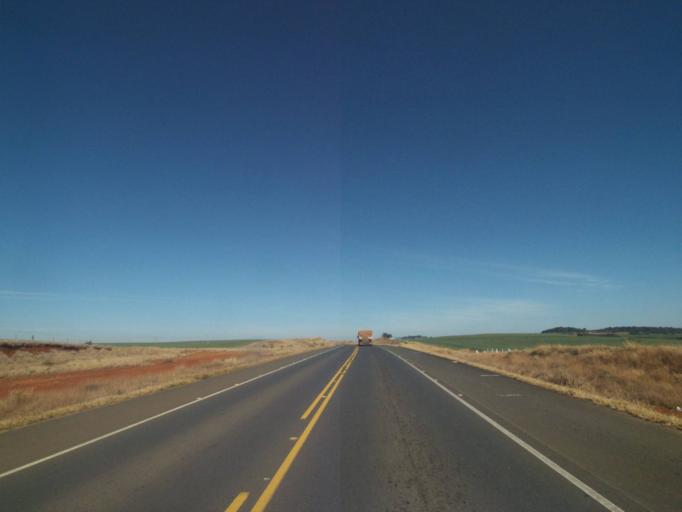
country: BR
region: Parana
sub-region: Tibagi
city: Tibagi
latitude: -24.6248
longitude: -50.4526
